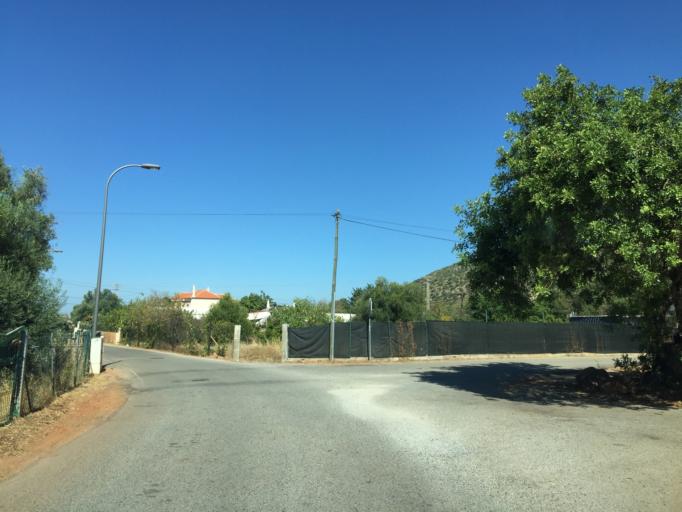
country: PT
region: Faro
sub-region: Loule
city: Almancil
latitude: 37.1053
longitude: -8.0590
